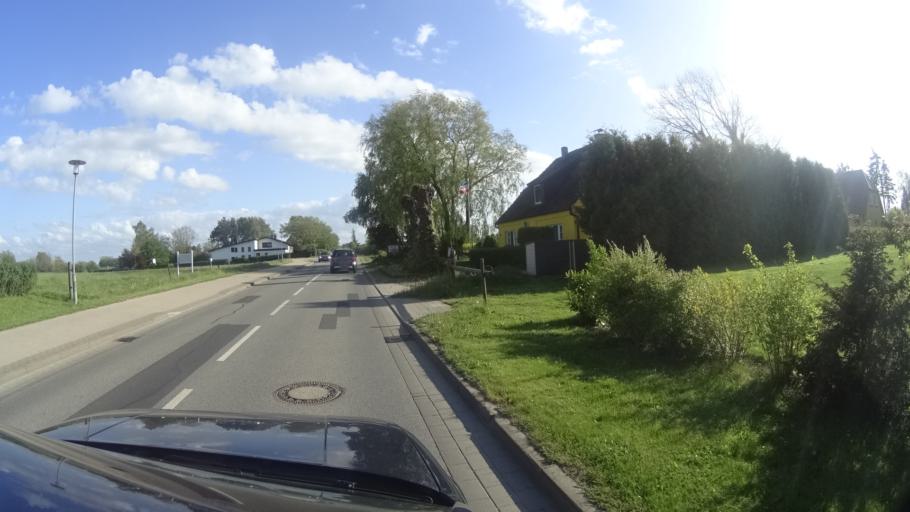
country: DE
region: Mecklenburg-Vorpommern
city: Ostseebad Dierhagen
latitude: 54.3595
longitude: 12.4094
